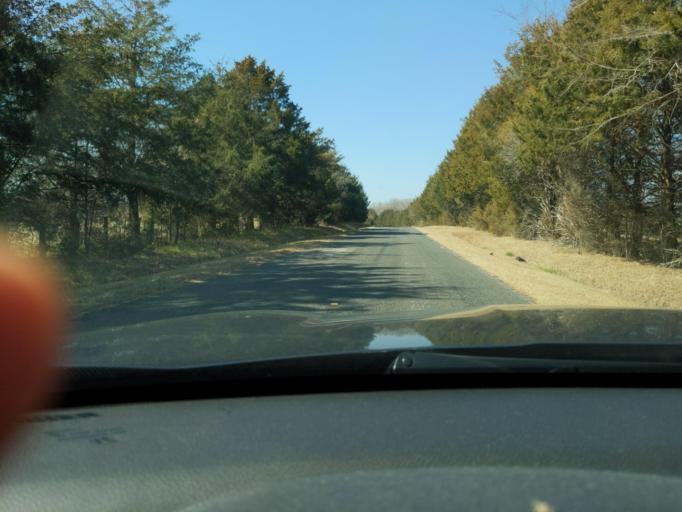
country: US
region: South Carolina
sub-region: Abbeville County
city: Calhoun Falls
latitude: 34.0860
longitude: -82.5501
